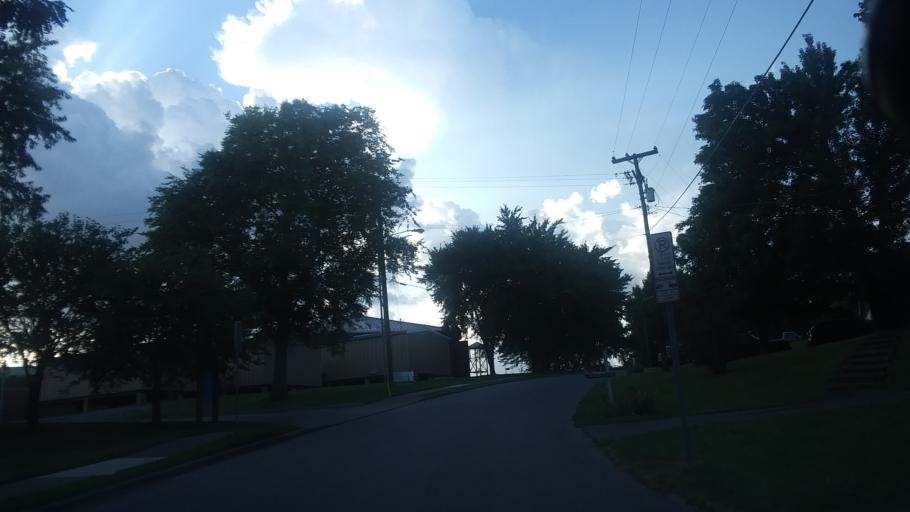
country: US
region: Tennessee
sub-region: Rutherford County
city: La Vergne
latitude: 36.0664
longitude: -86.6686
